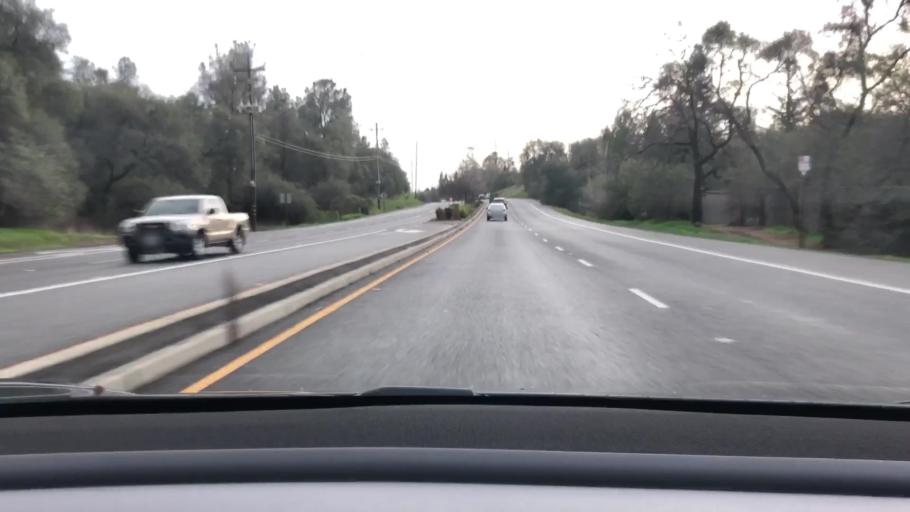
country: US
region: California
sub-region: Sacramento County
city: Folsom
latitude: 38.7188
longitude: -121.1756
